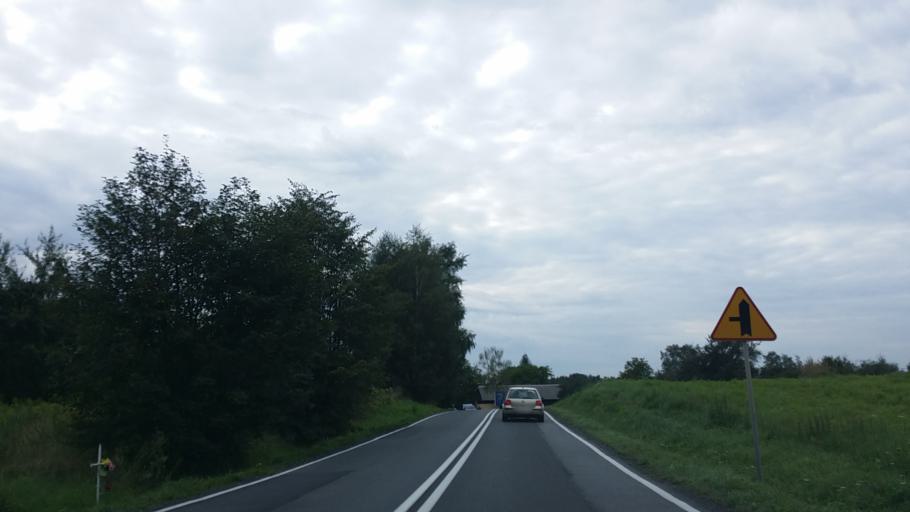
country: PL
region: Lesser Poland Voivodeship
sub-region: Powiat wadowicki
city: Brzeznica
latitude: 49.9620
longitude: 19.6526
